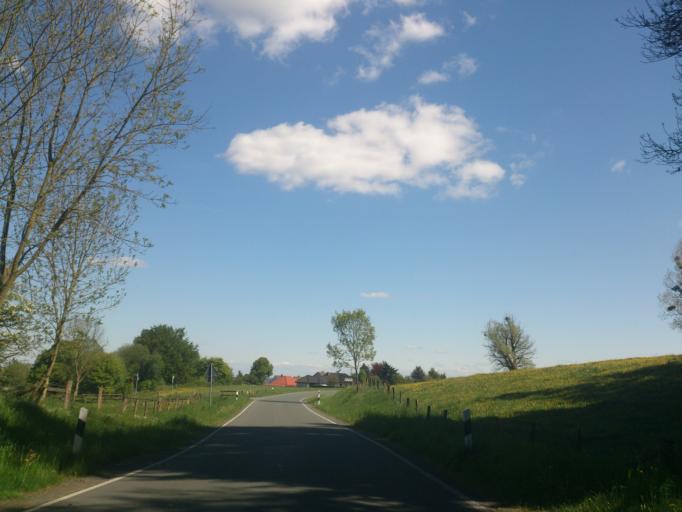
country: DE
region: North Rhine-Westphalia
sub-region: Regierungsbezirk Detmold
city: Willebadessen
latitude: 51.6534
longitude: 9.0413
